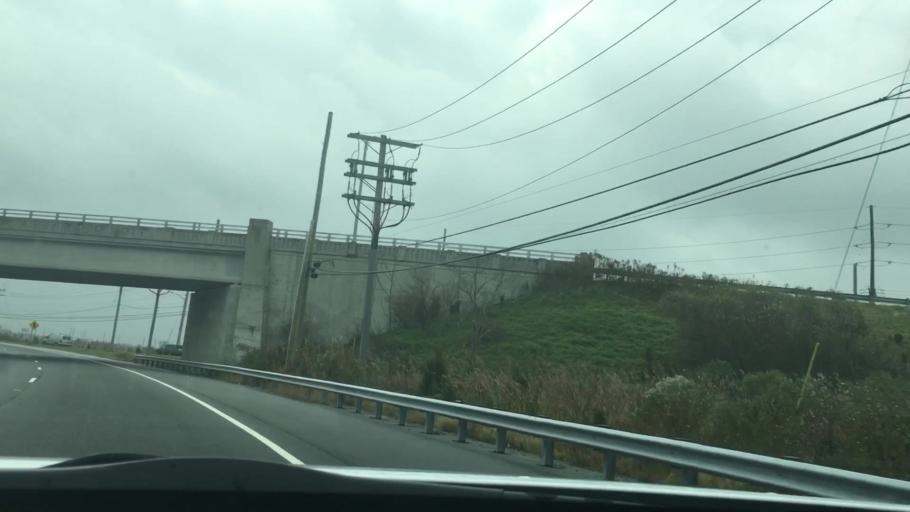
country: US
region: New Jersey
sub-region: Atlantic County
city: Absecon
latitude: 39.3967
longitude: -74.4927
